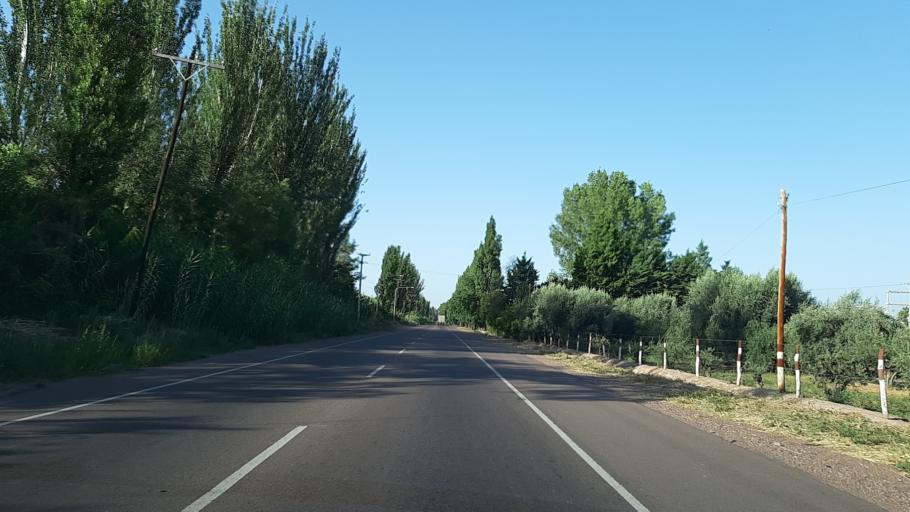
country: AR
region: Mendoza
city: San Martin
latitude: -33.0197
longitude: -68.4991
